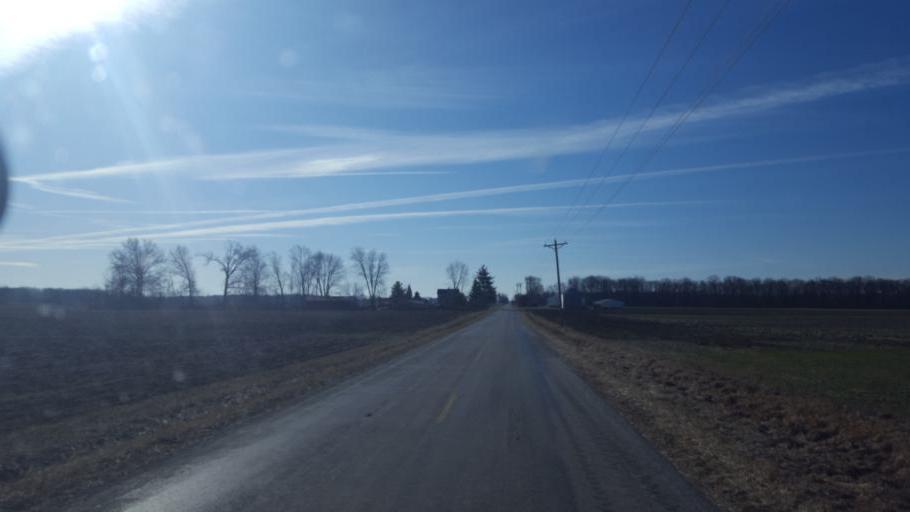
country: US
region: Ohio
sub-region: Morrow County
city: Cardington
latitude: 40.5469
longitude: -82.9957
